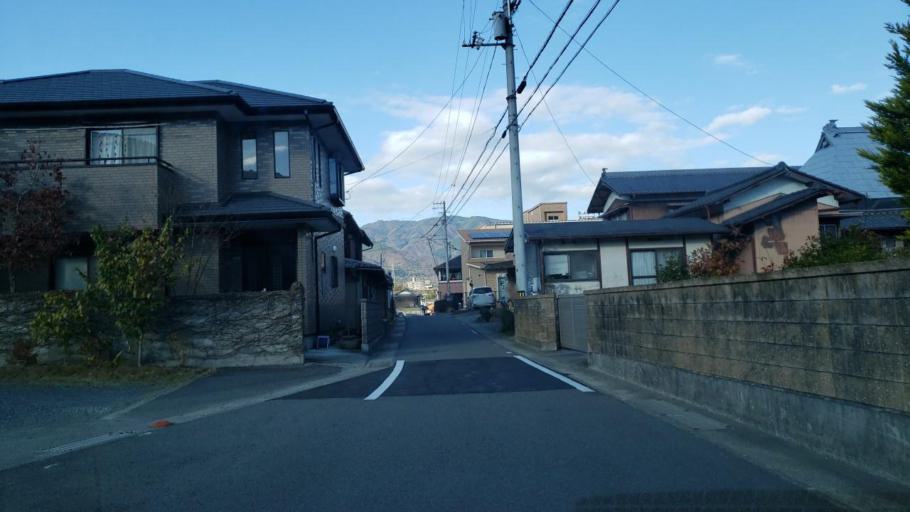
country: JP
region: Tokushima
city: Wakimachi
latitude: 34.0298
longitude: 134.0296
